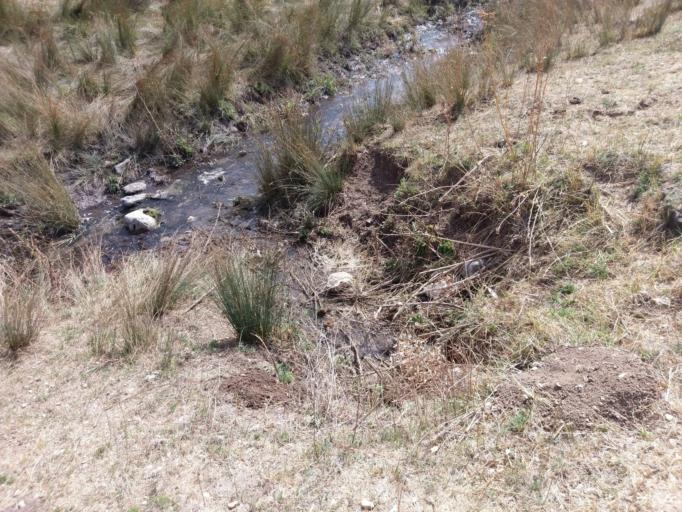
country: TR
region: Kayseri
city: Toklar
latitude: 38.4442
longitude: 36.0726
